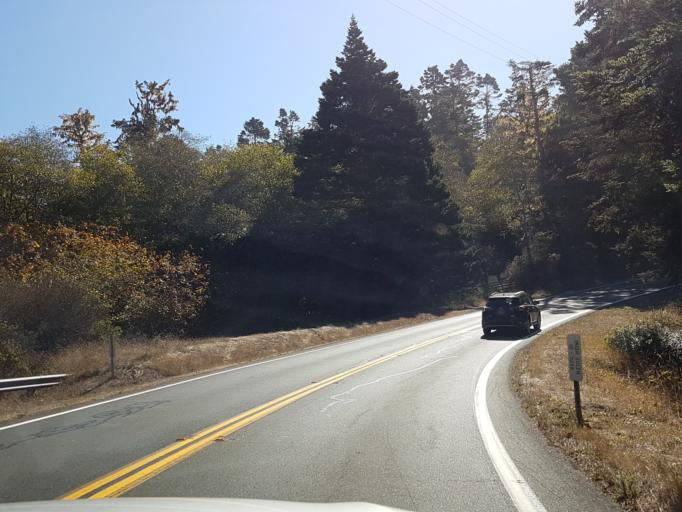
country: US
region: California
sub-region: Mendocino County
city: Boonville
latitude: 39.0212
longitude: -123.6855
